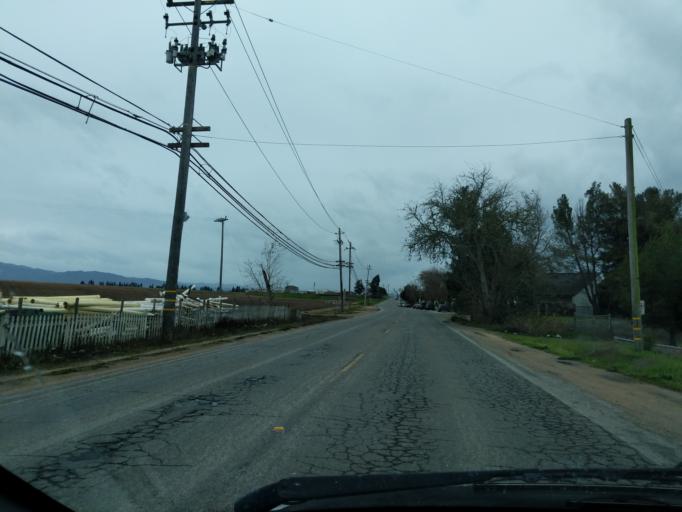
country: US
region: California
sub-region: Monterey County
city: Boronda
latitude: 36.7267
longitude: -121.6443
